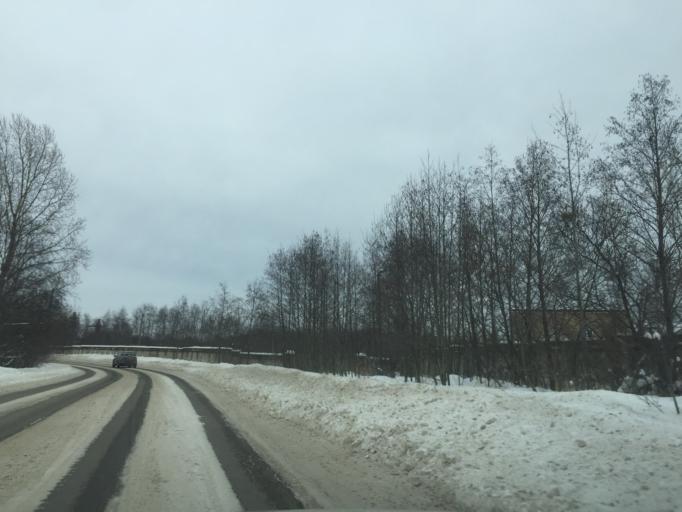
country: RU
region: Leningrad
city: Imeni Sverdlova
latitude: 59.7900
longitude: 30.6956
